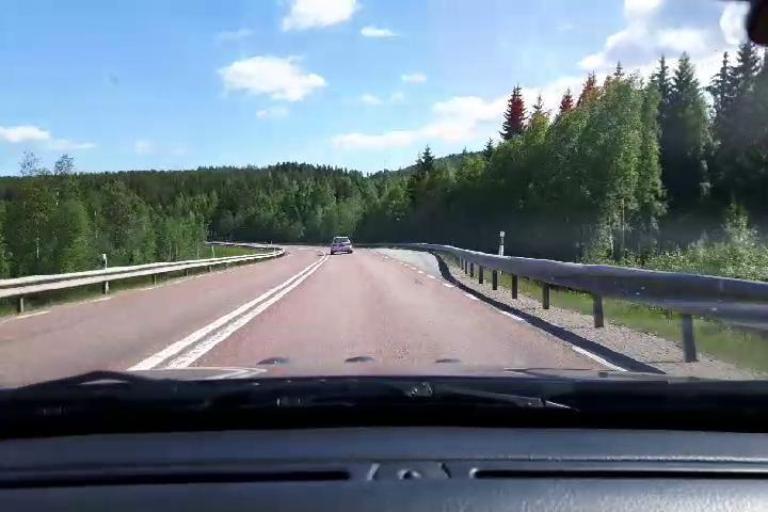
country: SE
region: Gaevleborg
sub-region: Hudiksvalls Kommun
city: Sorforsa
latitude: 61.7596
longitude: 16.7844
